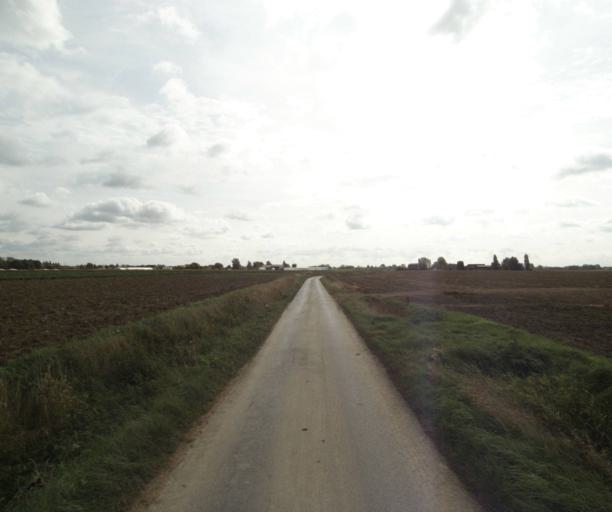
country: FR
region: Nord-Pas-de-Calais
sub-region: Departement du Nord
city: Bois-Grenier
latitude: 50.6506
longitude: 2.8543
